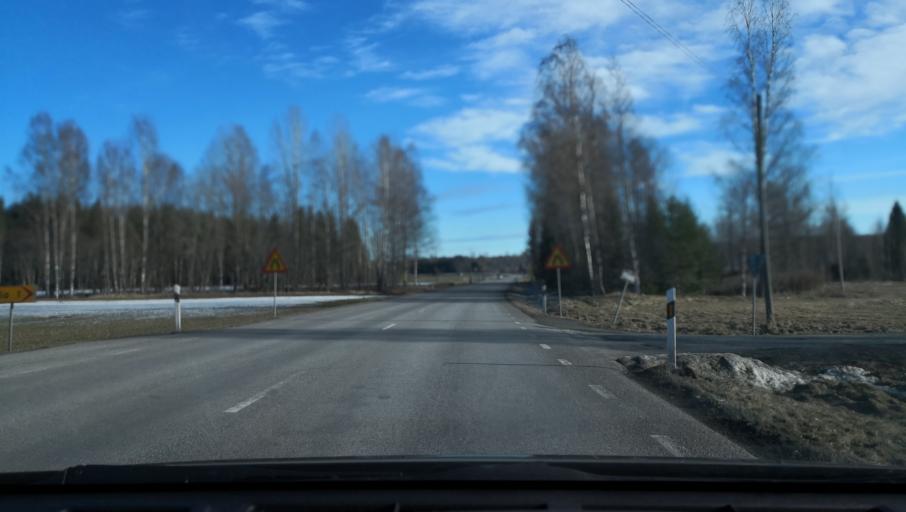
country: SE
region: Uppsala
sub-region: Osthammars Kommun
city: Osterbybruk
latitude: 60.1664
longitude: 17.9739
